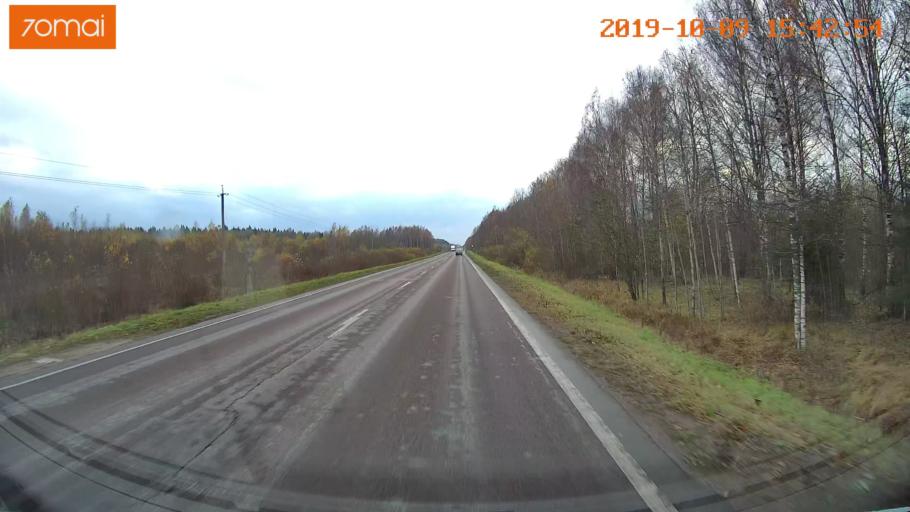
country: RU
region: Kostroma
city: Oktyabr'skiy
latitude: 57.8633
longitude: 41.0982
